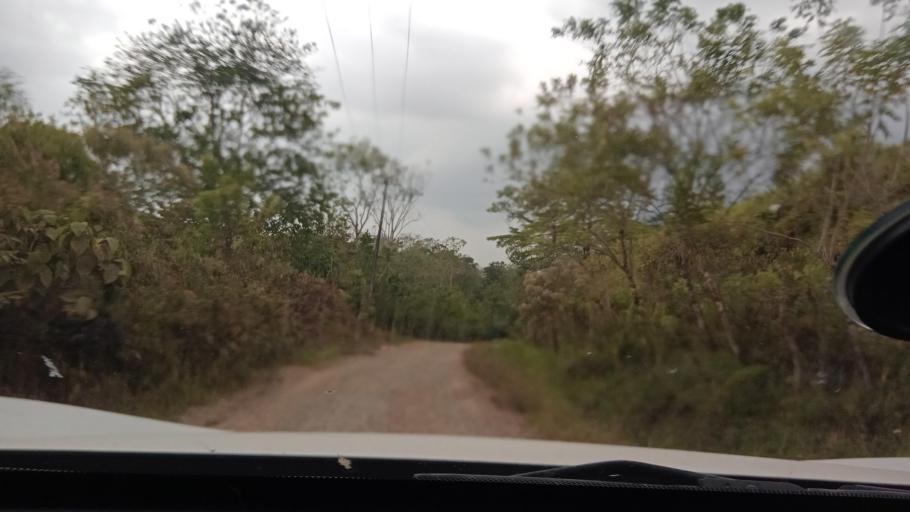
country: MX
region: Tabasco
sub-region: Huimanguillo
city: Francisco Rueda
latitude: 17.4320
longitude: -94.0438
